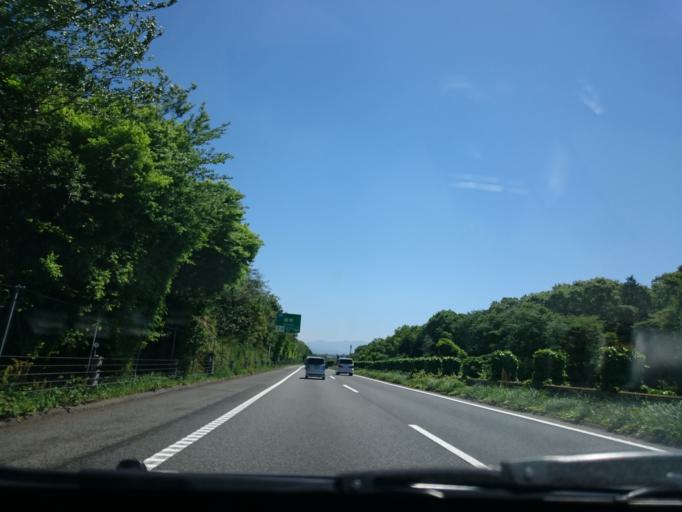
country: JP
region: Shizuoka
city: Gotemba
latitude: 35.2336
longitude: 138.9095
